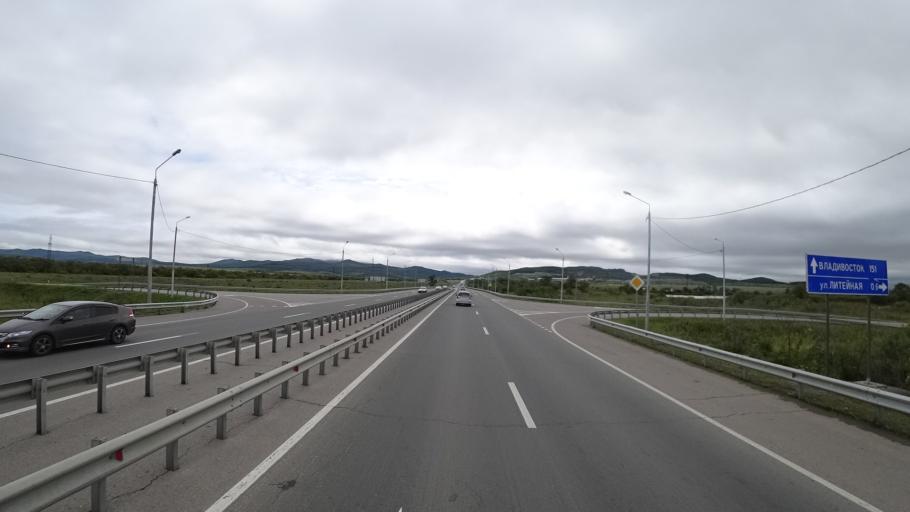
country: RU
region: Primorskiy
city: Monastyrishche
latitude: 44.1849
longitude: 132.4415
